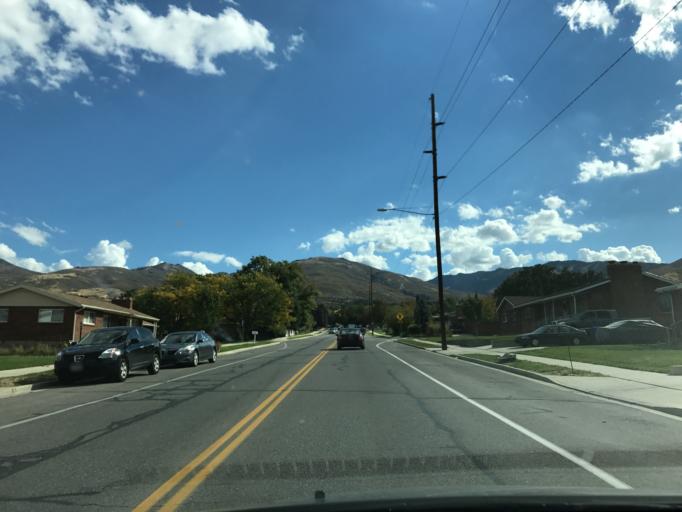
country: US
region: Utah
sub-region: Davis County
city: Woods Cross
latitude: 40.8711
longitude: -111.8799
